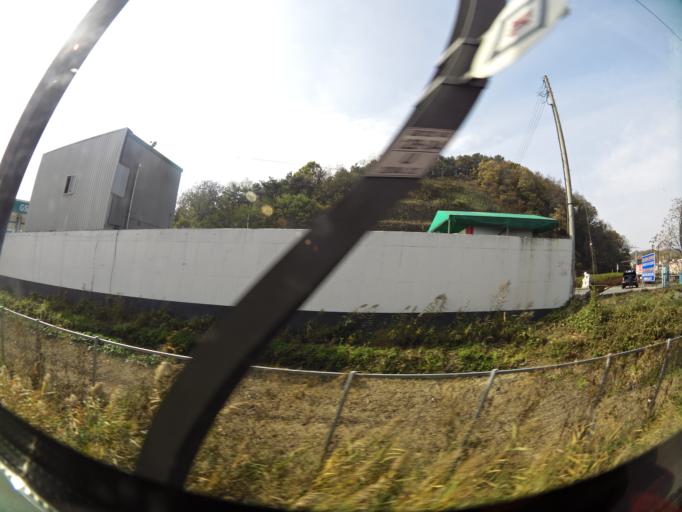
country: KR
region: Chungcheongbuk-do
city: Cheongju-si
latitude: 36.6160
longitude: 127.2931
